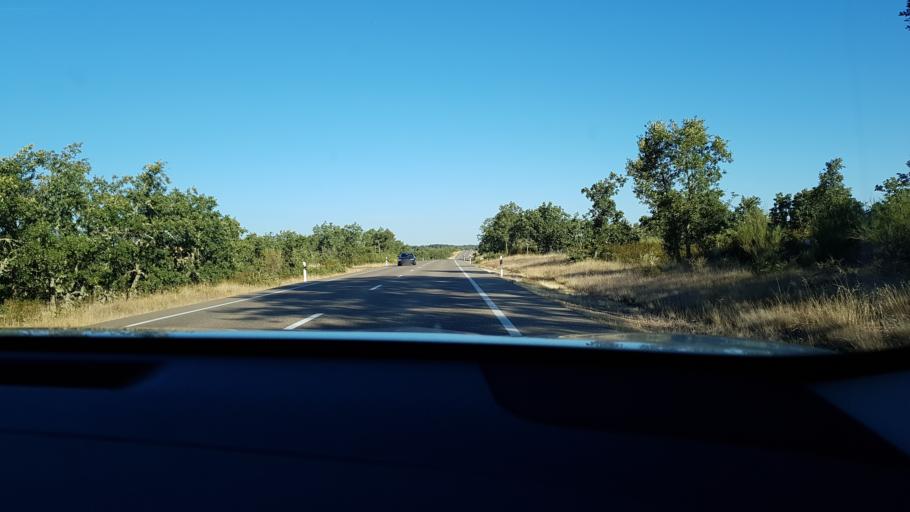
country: ES
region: Castille and Leon
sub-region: Provincia de Zamora
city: Samir de los Canos
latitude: 41.6630
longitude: -6.2093
